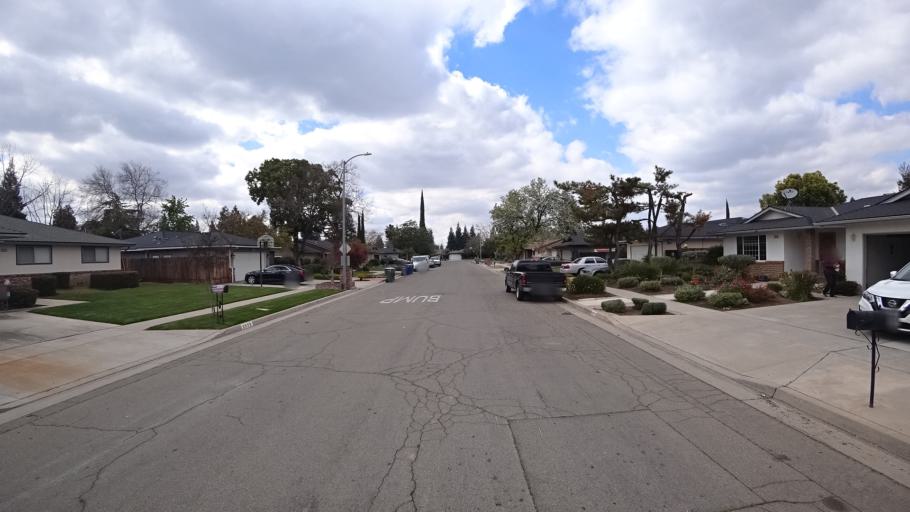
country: US
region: California
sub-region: Fresno County
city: Fresno
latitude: 36.8348
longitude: -119.8099
